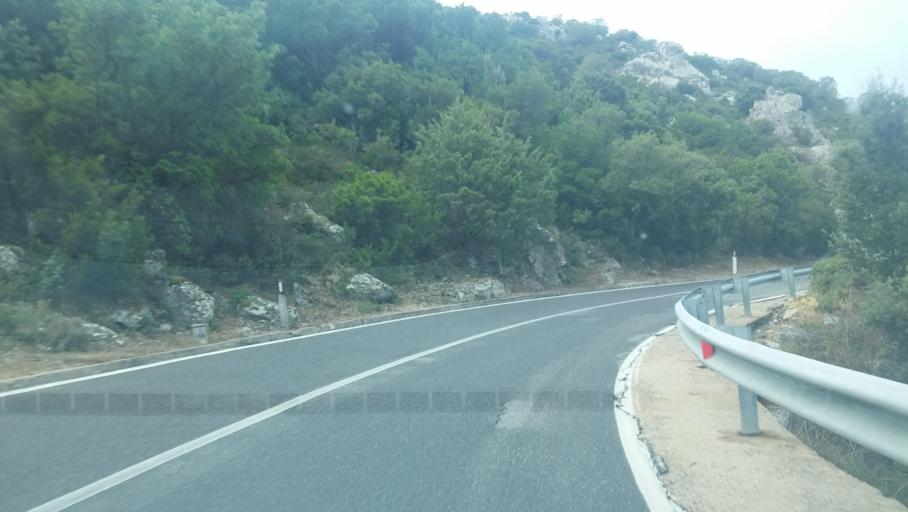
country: IT
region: Sardinia
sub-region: Provincia di Ogliastra
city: Urzulei
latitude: 40.1791
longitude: 9.5326
